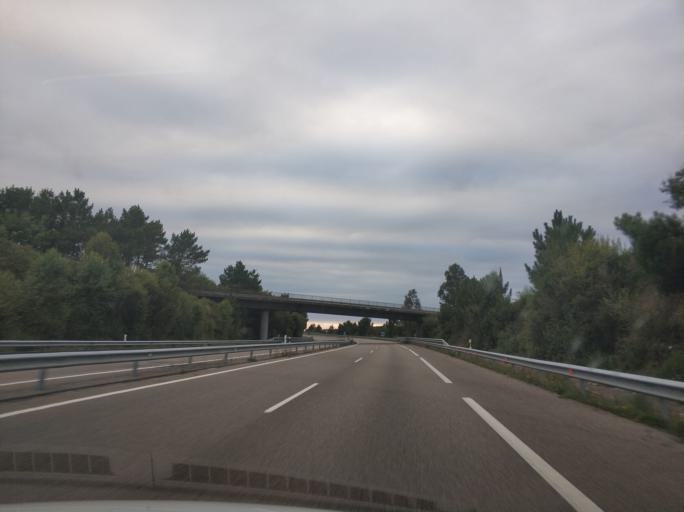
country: ES
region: Asturias
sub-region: Province of Asturias
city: Tineo
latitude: 43.5475
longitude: -6.4586
